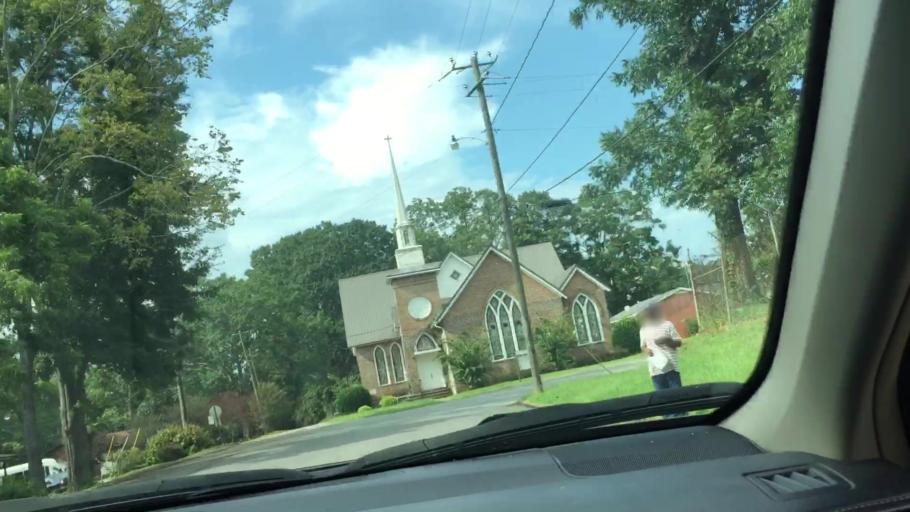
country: US
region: Alabama
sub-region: Hale County
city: Greensboro
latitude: 32.7068
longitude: -87.5893
